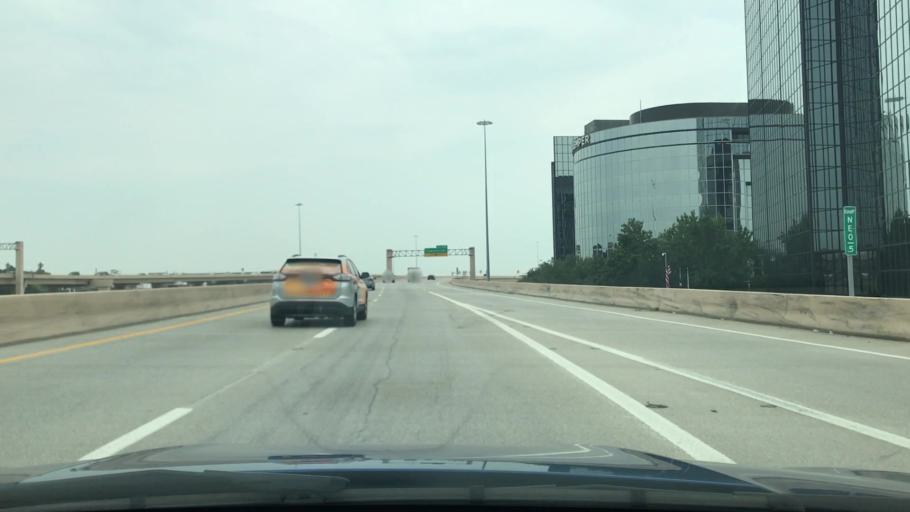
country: US
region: Texas
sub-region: Dallas County
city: Richardson
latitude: 32.9236
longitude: -96.7604
